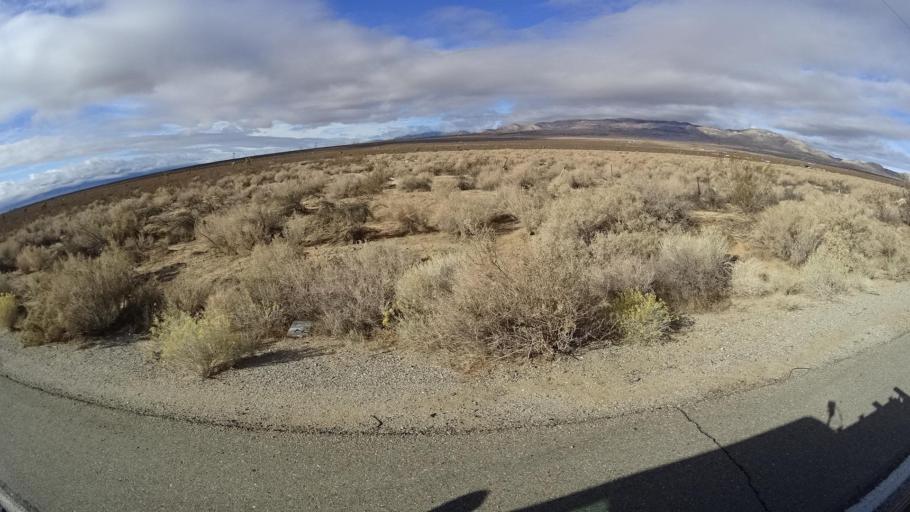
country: US
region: California
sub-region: Kern County
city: Mojave
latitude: 34.9558
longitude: -118.2918
